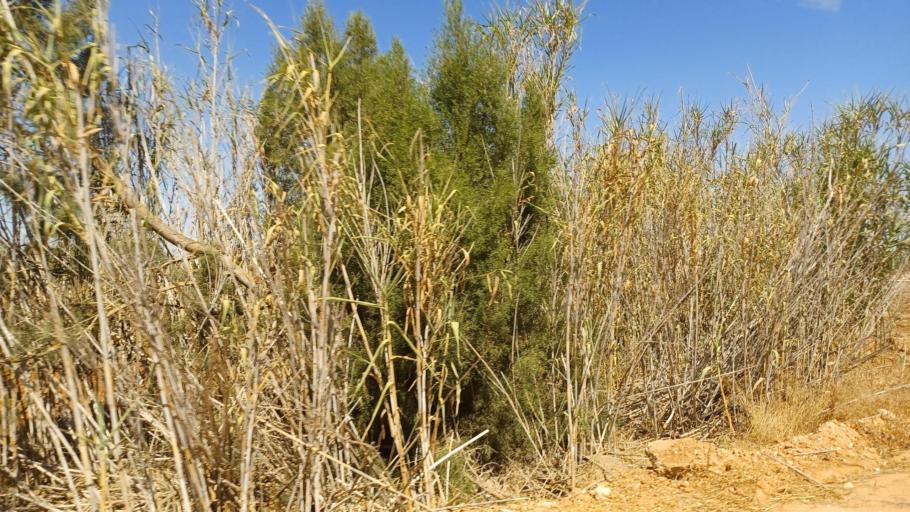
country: CY
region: Ammochostos
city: Avgorou
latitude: 35.0619
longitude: 33.8294
